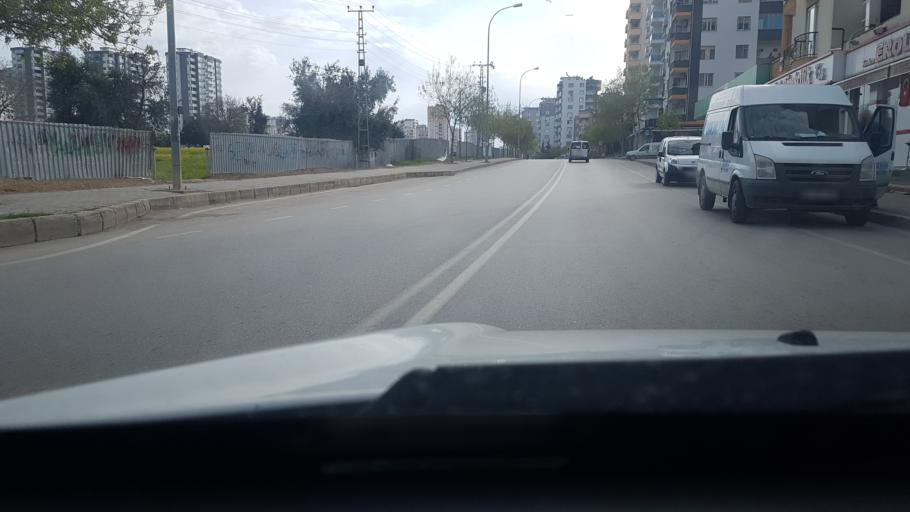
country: TR
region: Adana
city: Seyhan
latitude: 37.0343
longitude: 35.2741
